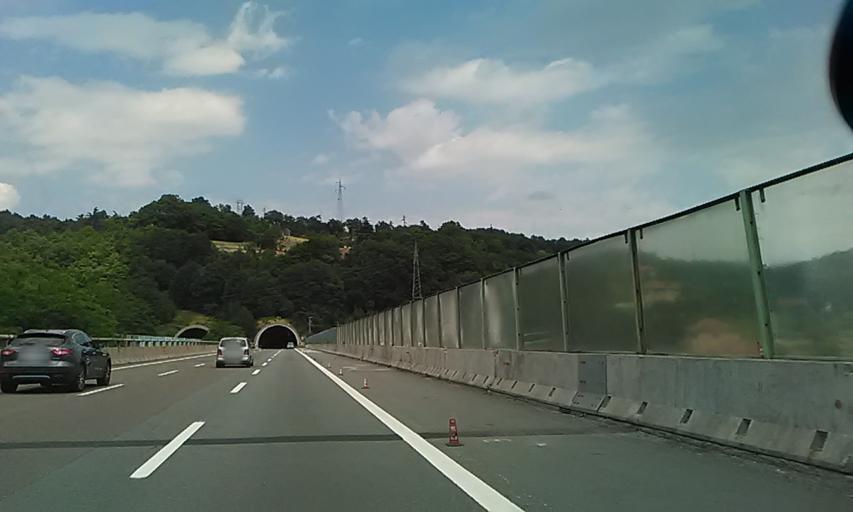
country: IT
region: Liguria
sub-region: Provincia di Genova
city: Rossiglione
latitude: 44.5668
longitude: 8.6622
